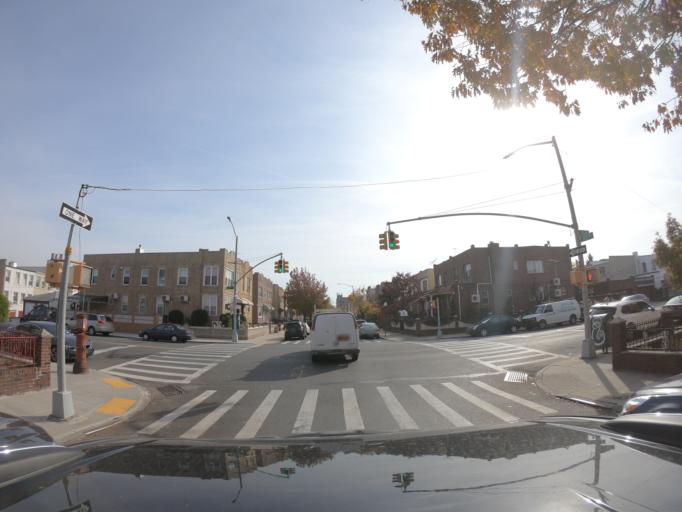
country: US
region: New York
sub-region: Kings County
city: Bensonhurst
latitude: 40.6170
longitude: -73.9820
